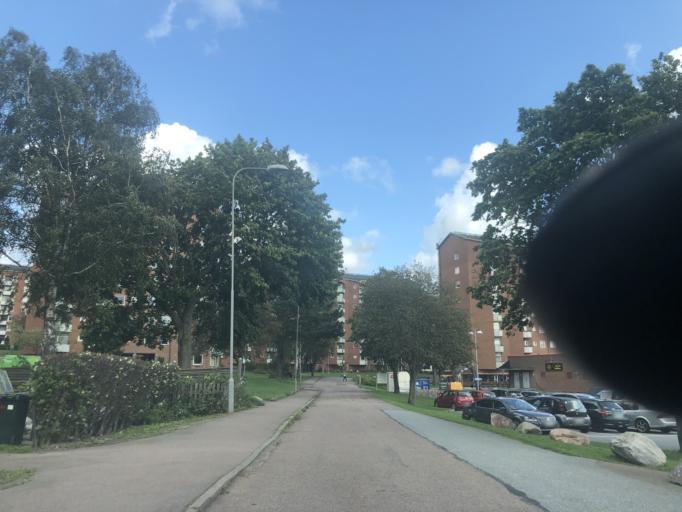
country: SE
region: Vaestra Goetaland
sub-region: Goteborg
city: Goeteborg
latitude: 57.7292
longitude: 11.9698
